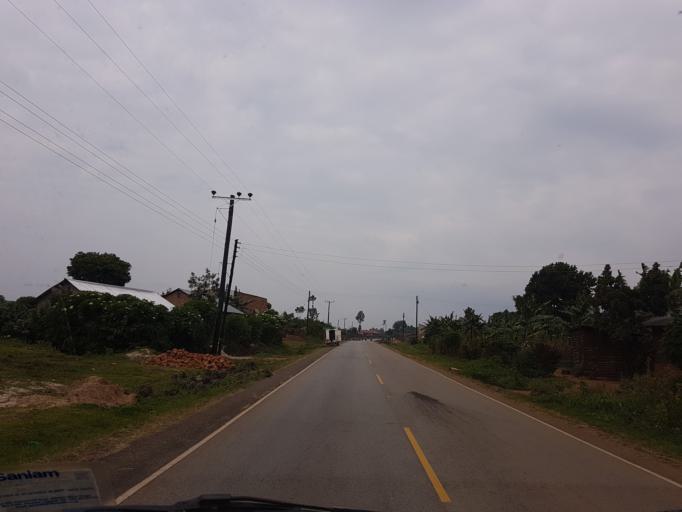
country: UG
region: Western Region
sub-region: Kisoro District
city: Kisoro
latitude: -1.3025
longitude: 29.7234
